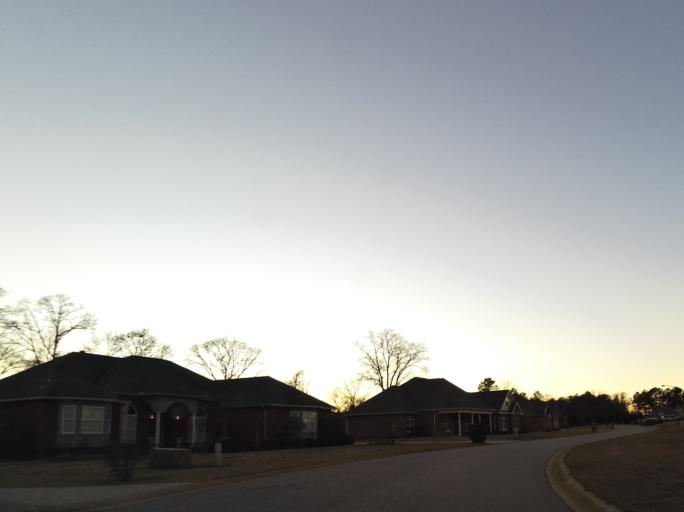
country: US
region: Georgia
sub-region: Peach County
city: Byron
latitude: 32.6027
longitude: -83.7690
